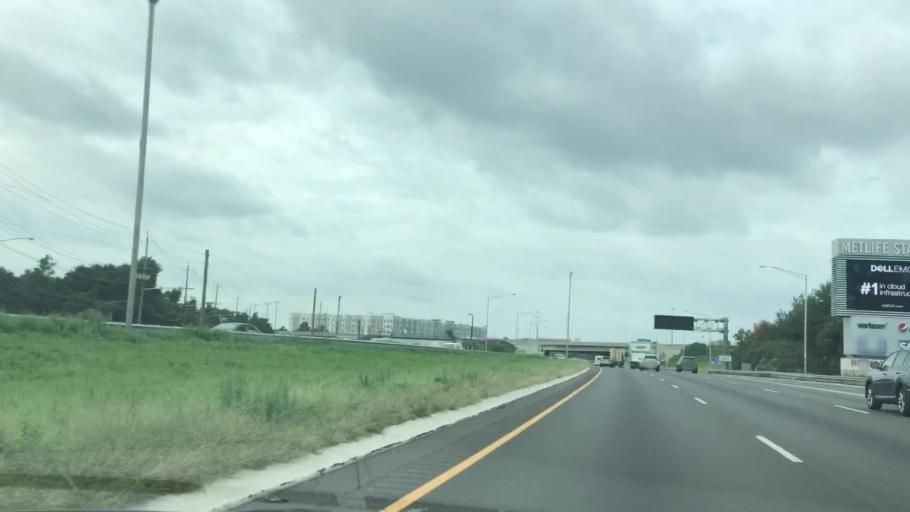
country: US
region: New Jersey
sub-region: Hudson County
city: Secaucus
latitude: 40.8069
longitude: -74.0760
